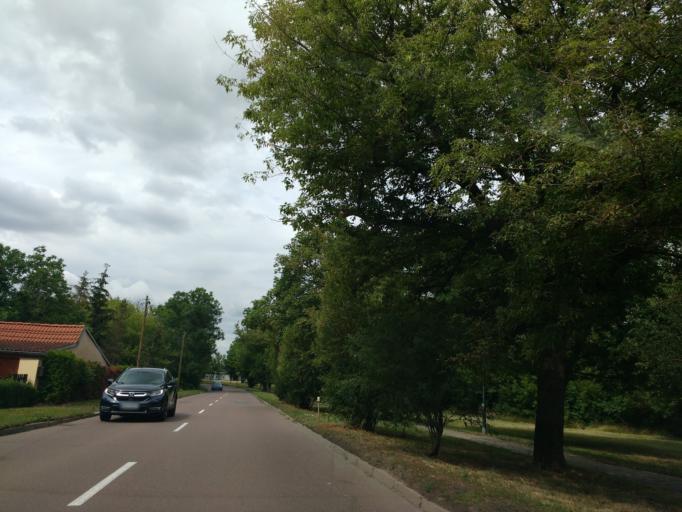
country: DE
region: Saxony-Anhalt
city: Dieskau
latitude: 51.4328
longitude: 12.0434
